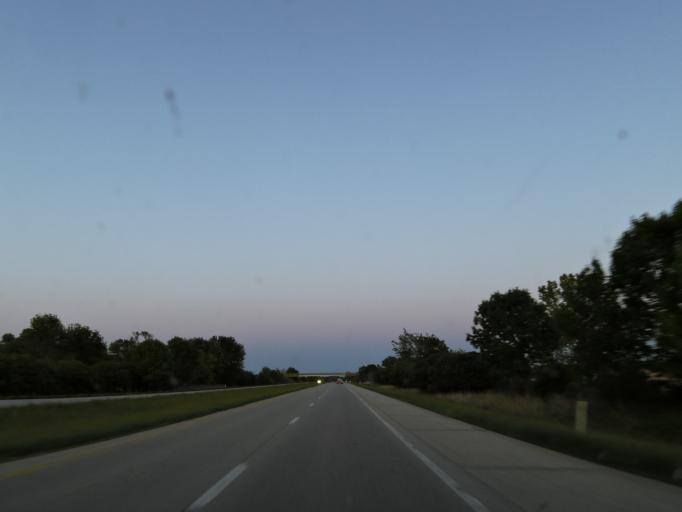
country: US
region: Indiana
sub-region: Boone County
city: Thorntown
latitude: 39.9807
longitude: -86.6811
